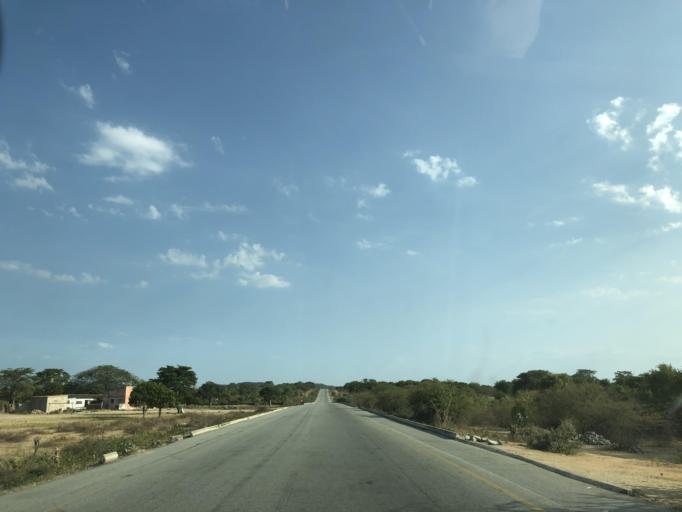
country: AO
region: Benguela
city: Benguela
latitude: -13.2158
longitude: 13.7657
